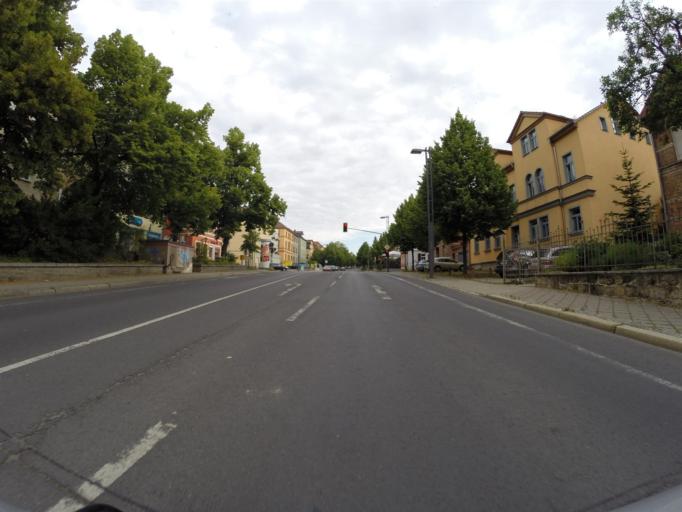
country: DE
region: Thuringia
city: Weimar
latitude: 50.9880
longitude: 11.3296
